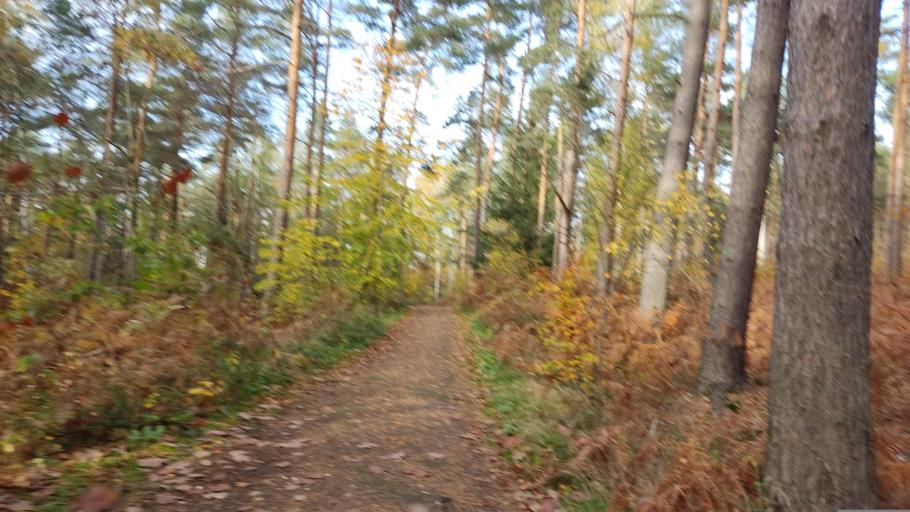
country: DE
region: Saxony
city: Struppen
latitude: 50.8969
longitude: 14.0329
